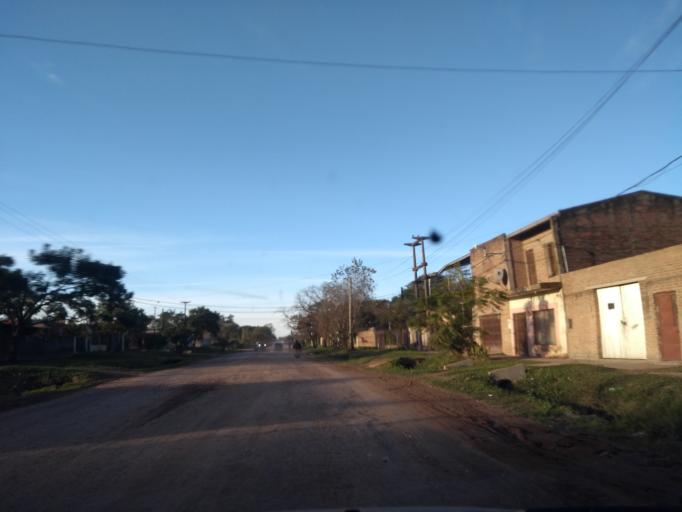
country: AR
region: Chaco
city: Resistencia
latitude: -27.4914
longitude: -58.9743
